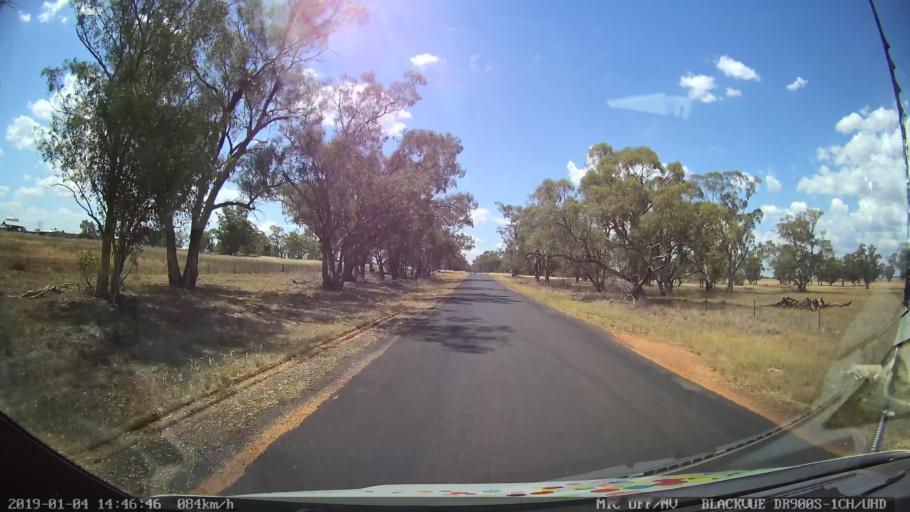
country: AU
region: New South Wales
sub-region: Dubbo Municipality
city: Dubbo
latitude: -32.0774
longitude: 148.6589
